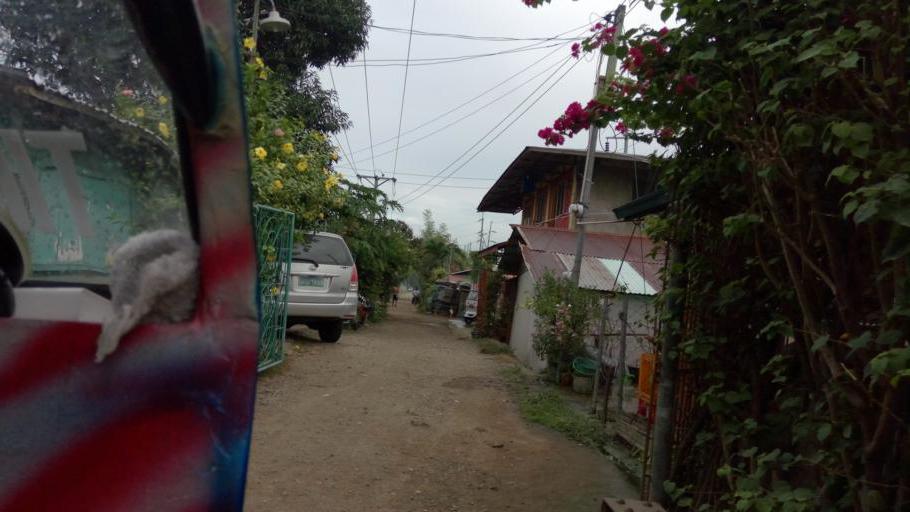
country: PH
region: Ilocos
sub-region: Province of La Union
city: Paringao
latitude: 16.5545
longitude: 120.3255
